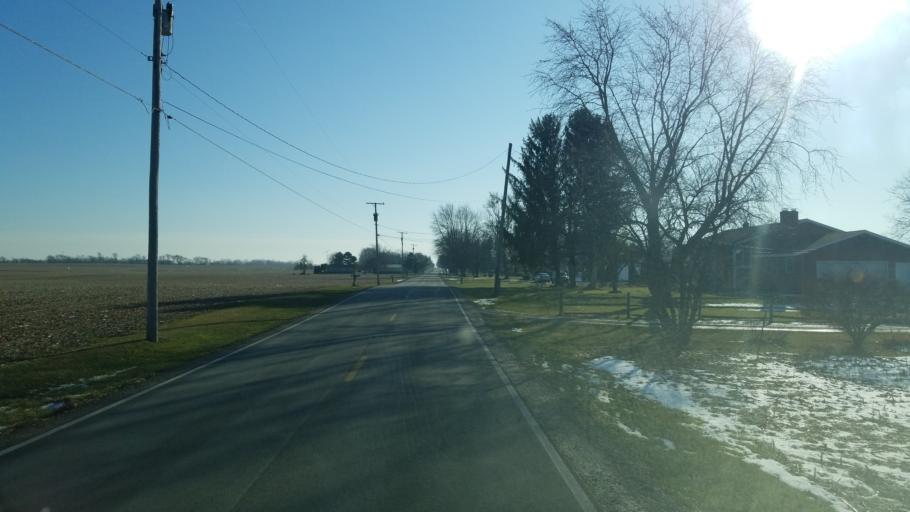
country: US
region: Ohio
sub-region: Huron County
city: Bellevue
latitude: 41.3030
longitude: -82.8787
